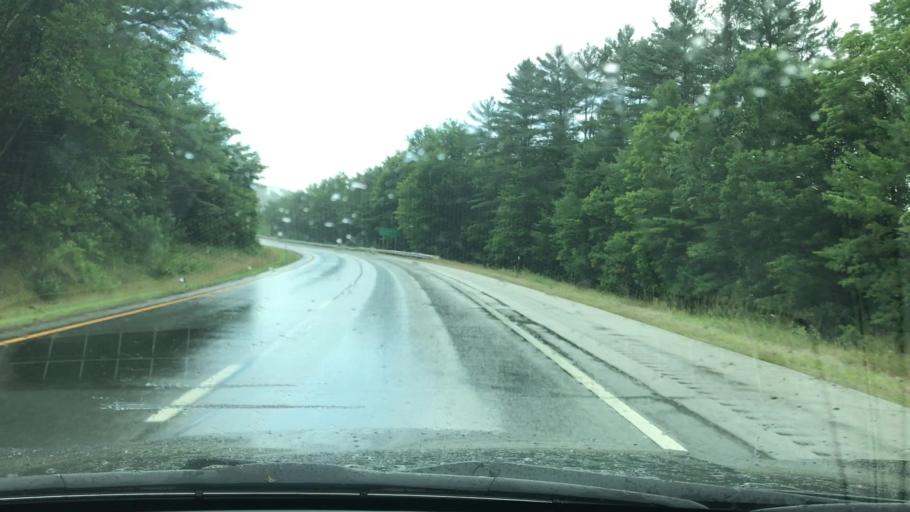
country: US
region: New Hampshire
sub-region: Grafton County
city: Littleton
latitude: 44.3028
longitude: -71.7767
